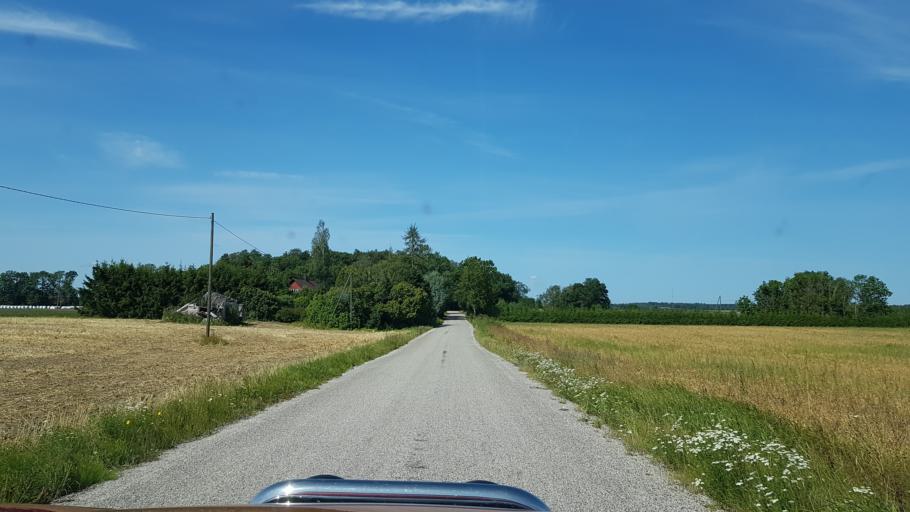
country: EE
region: Jaervamaa
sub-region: Jaerva-Jaani vald
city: Jarva-Jaani
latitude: 59.0881
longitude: 25.7350
